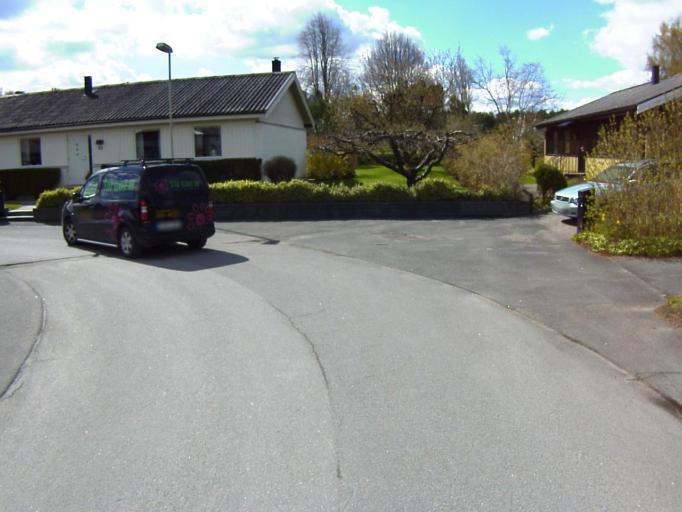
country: SE
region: Skane
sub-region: Kristianstads Kommun
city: Norra Asum
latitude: 56.0070
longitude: 14.0963
